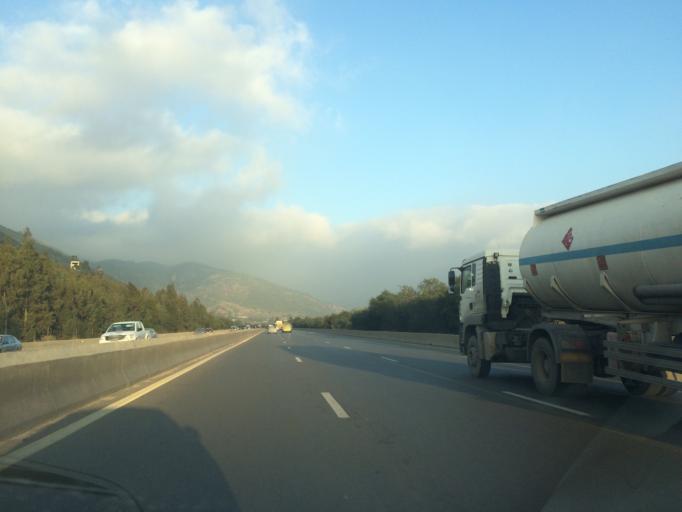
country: DZ
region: Tipaza
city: Hadjout
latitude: 36.3832
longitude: 2.4853
